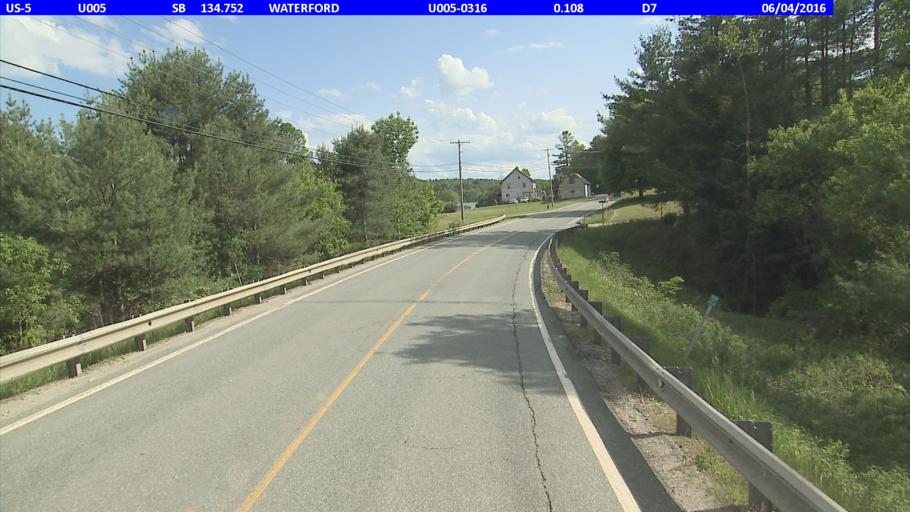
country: US
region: Vermont
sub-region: Caledonia County
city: Saint Johnsbury
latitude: 44.3808
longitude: -72.0262
